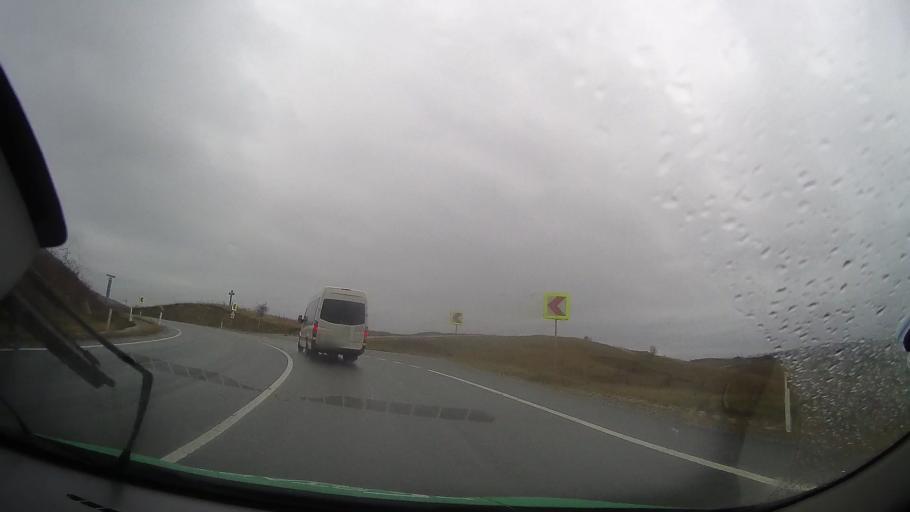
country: RO
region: Bistrita-Nasaud
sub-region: Comuna Galatii Bistritei
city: Galatii Bistritei
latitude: 47.0330
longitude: 24.4210
